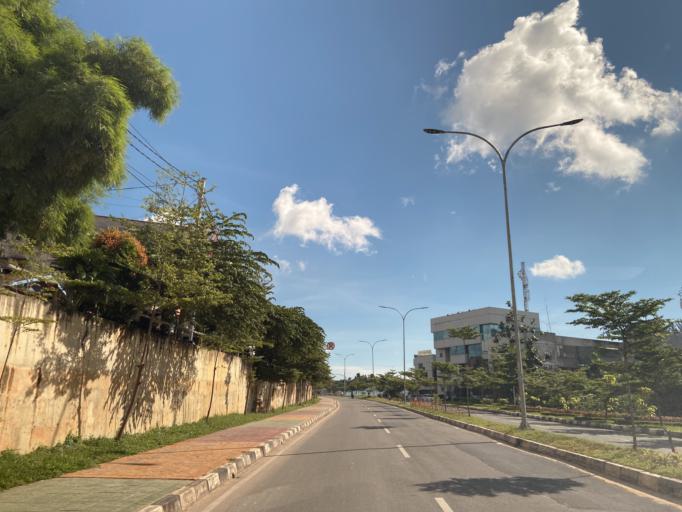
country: SG
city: Singapore
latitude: 1.1429
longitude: 104.0175
